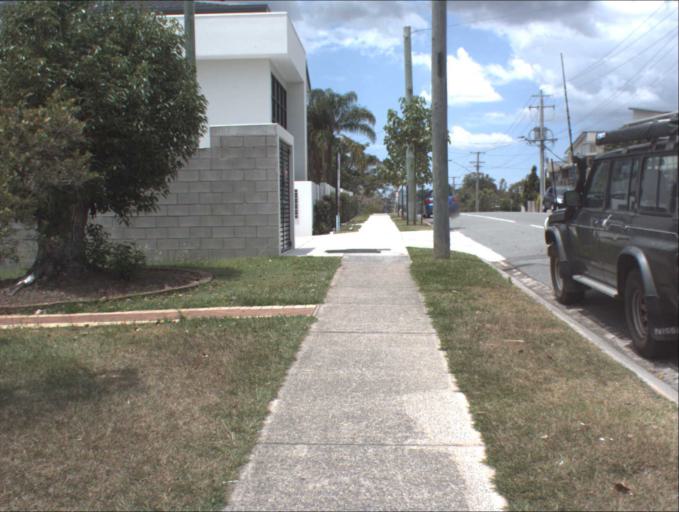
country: AU
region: Queensland
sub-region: Logan
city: Beenleigh
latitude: -27.7204
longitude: 153.2053
